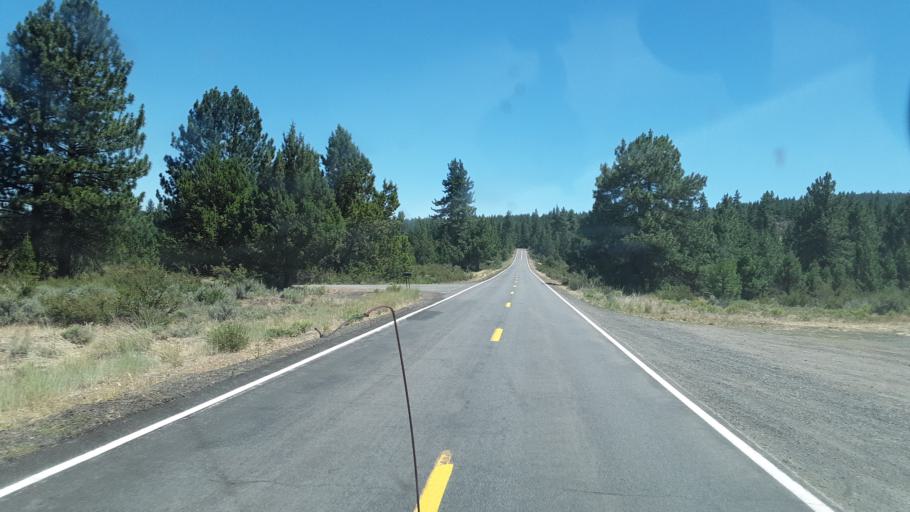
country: US
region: California
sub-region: Lassen County
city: Johnstonville
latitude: 40.4969
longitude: -120.5607
